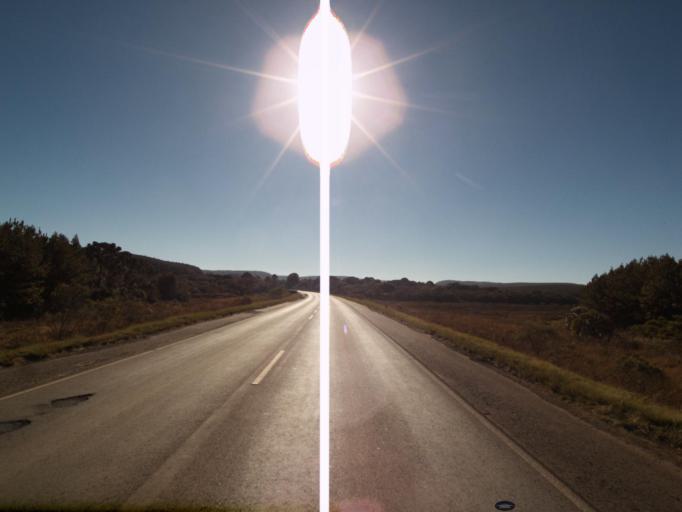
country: BR
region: Santa Catarina
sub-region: Concordia
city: Concordia
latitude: -26.9338
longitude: -51.8151
